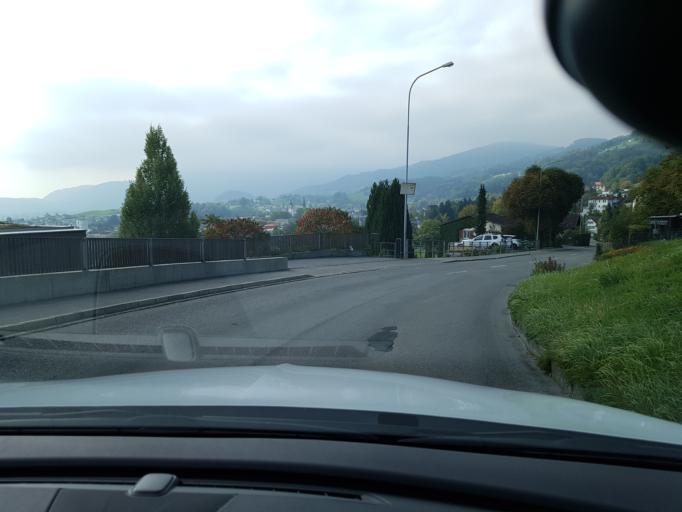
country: CH
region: Saint Gallen
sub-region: Wahlkreis Rheintal
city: Altstatten
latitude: 47.3874
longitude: 9.5483
